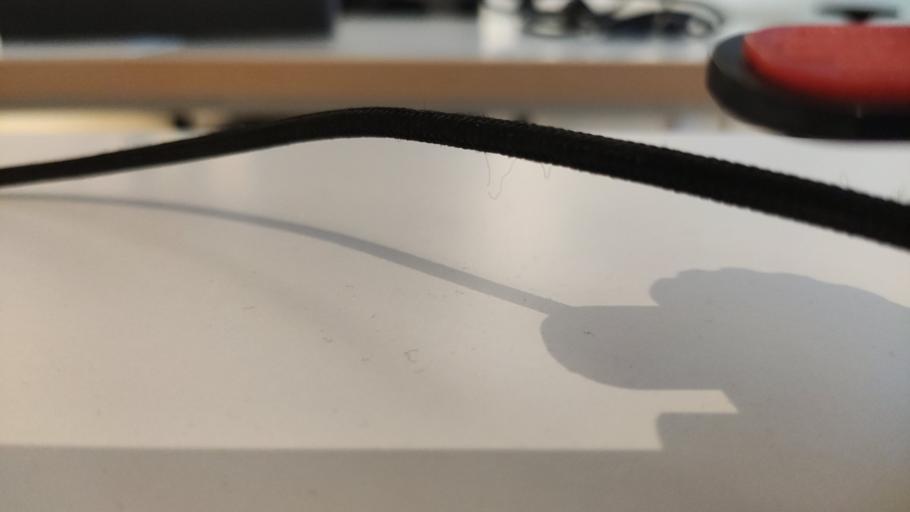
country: RU
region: Moskovskaya
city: Ruza
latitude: 55.8061
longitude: 36.2927
